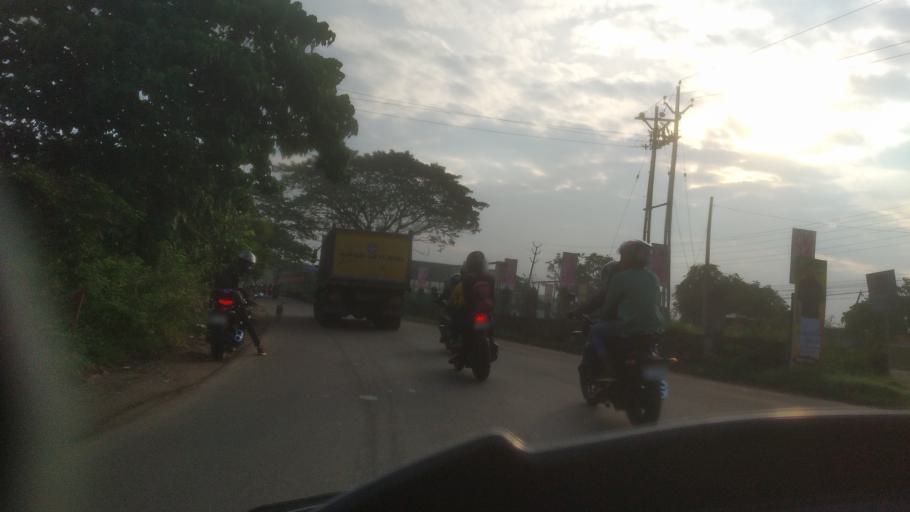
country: IN
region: Kerala
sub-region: Ernakulam
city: Perumpavur
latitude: 10.1142
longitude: 76.4644
